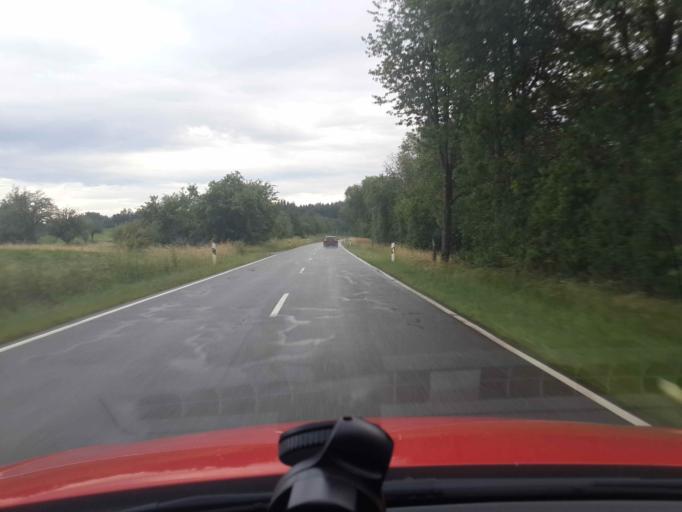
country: DE
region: Baden-Wuerttemberg
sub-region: Karlsruhe Region
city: Limbach
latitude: 49.4519
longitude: 9.2126
